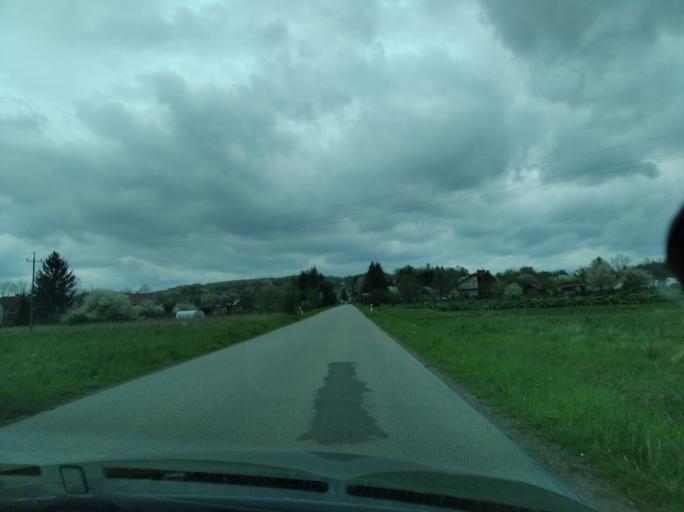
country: PL
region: Subcarpathian Voivodeship
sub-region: Powiat sanocki
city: Dlugie
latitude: 49.6012
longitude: 22.0520
